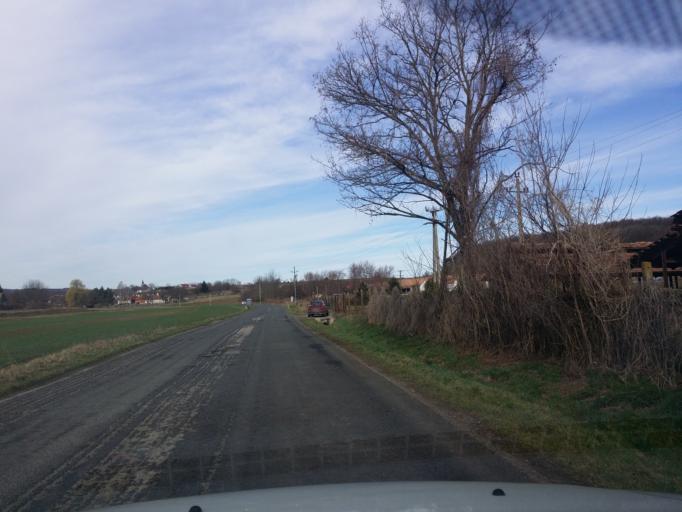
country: HU
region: Baranya
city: Villany
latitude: 45.8788
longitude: 18.4386
